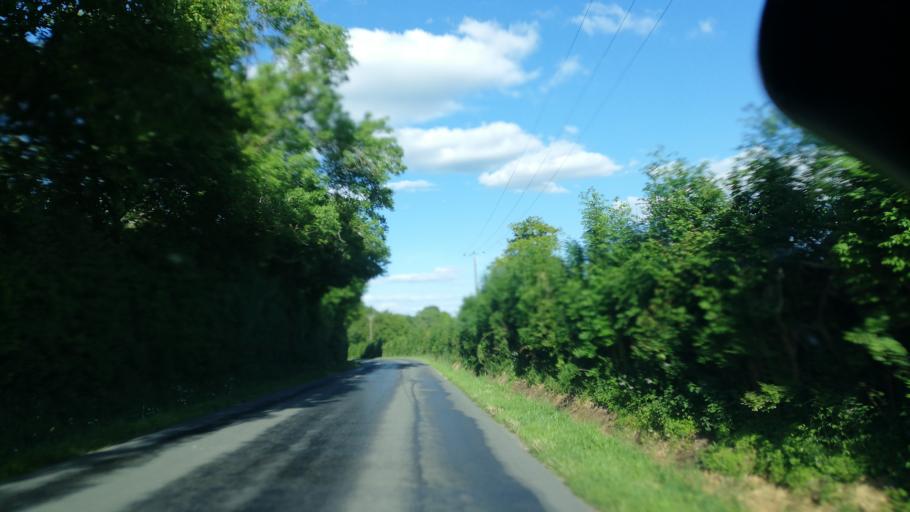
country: FR
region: Poitou-Charentes
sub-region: Departement des Deux-Sevres
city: Boisme
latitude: 46.7683
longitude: -0.4490
